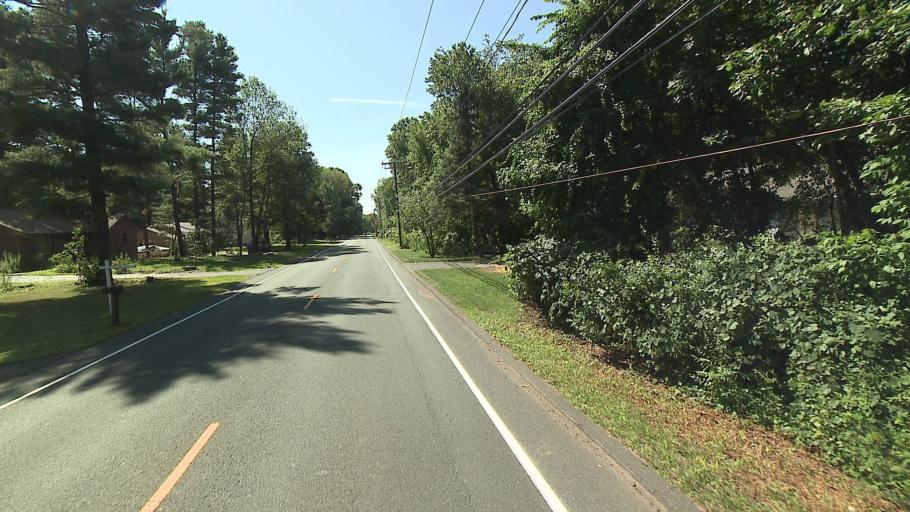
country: US
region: Connecticut
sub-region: Hartford County
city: Blue Hills
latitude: 41.8501
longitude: -72.7018
